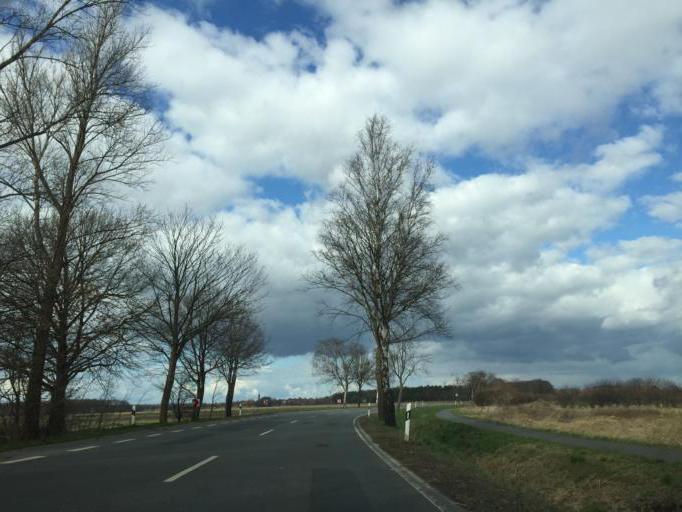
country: DE
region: Lower Saxony
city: Edemissen
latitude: 52.3725
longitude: 10.2494
